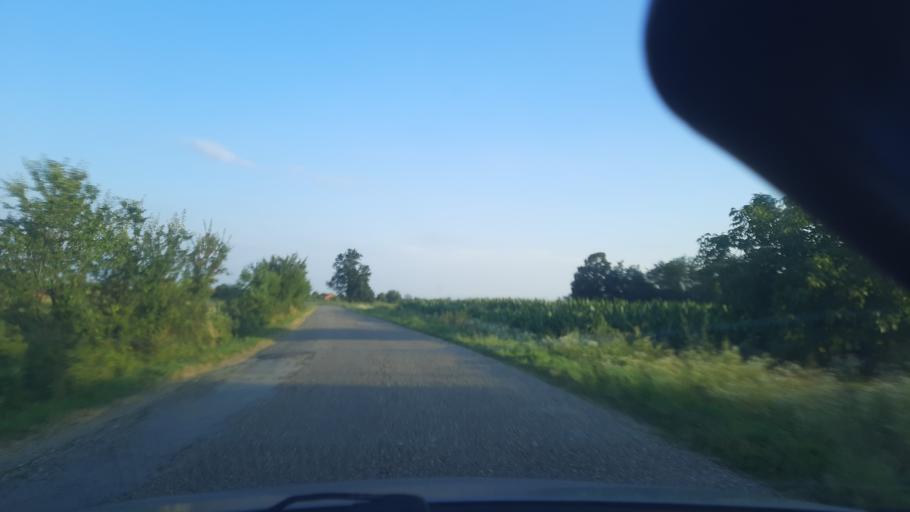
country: RS
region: Central Serbia
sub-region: Macvanski Okrug
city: Vladimirci
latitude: 44.6398
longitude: 19.8394
